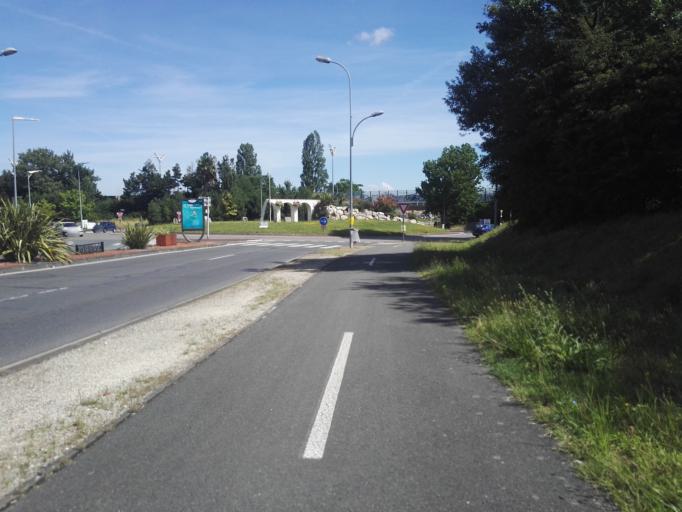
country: FR
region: Aquitaine
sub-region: Departement de la Gironde
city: Villenave-d'Ornon
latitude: 44.7777
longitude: -0.5702
